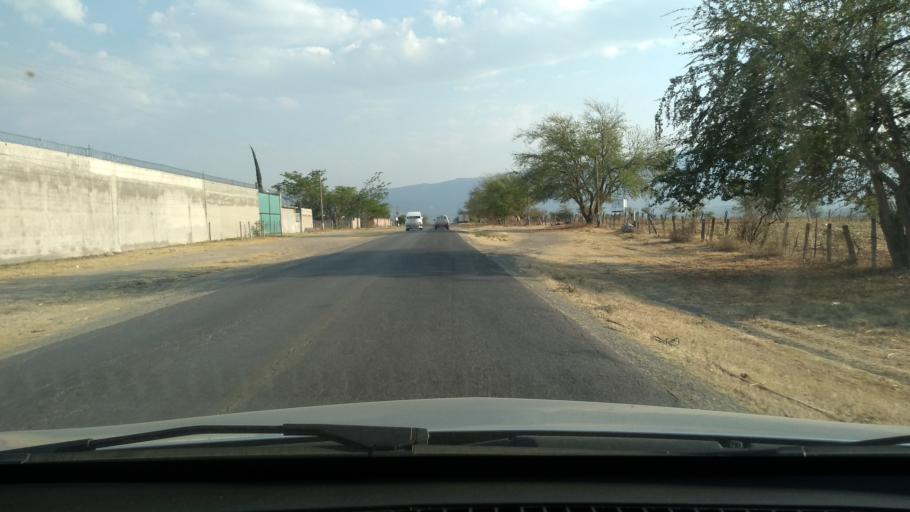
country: MX
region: Morelos
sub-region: Jojutla
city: Tehuixtla
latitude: 18.5802
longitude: -99.2641
